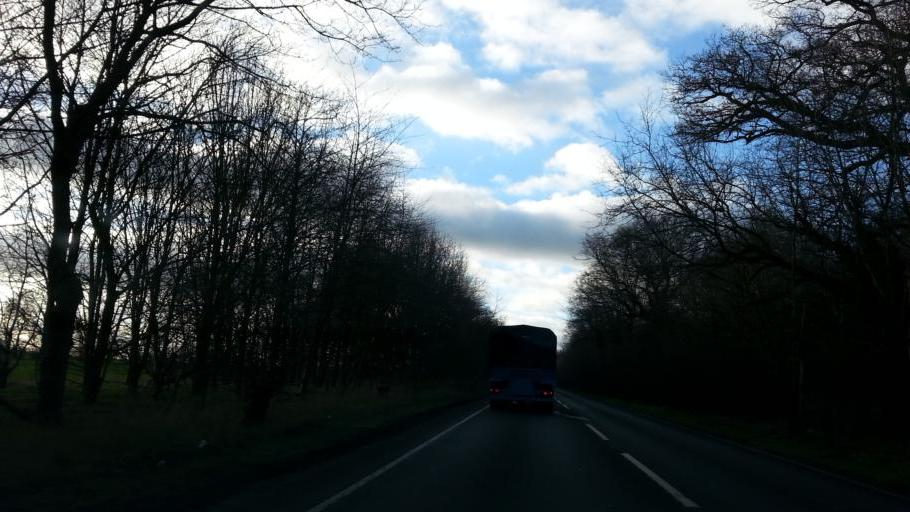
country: GB
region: England
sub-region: Norfolk
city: Harleston
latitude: 52.3666
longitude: 1.2274
